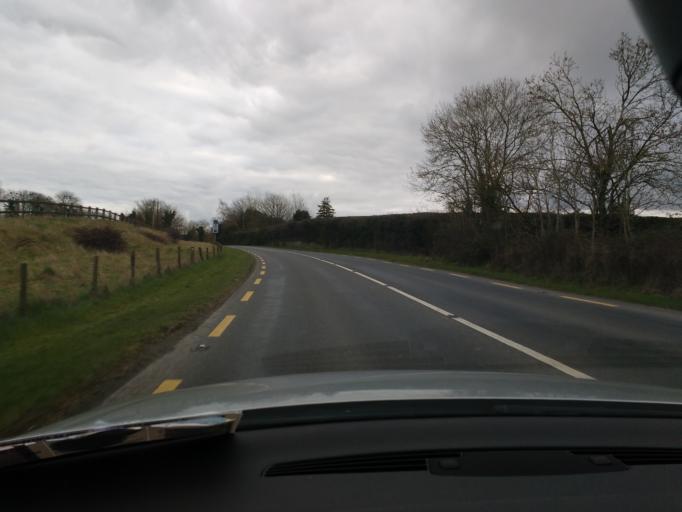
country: IE
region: Leinster
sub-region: Kilkenny
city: Kilkenny
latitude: 52.6773
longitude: -7.2750
